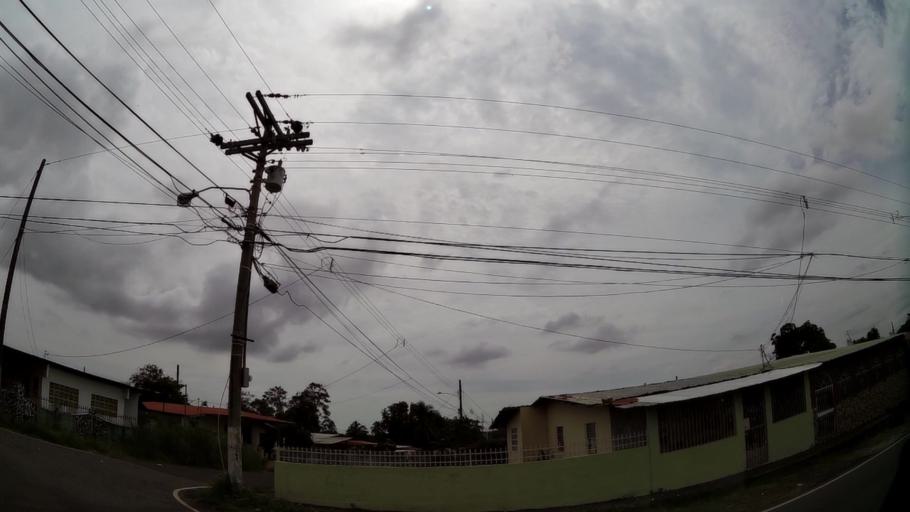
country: PA
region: Panama
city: San Miguelito
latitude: 9.0413
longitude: -79.4301
